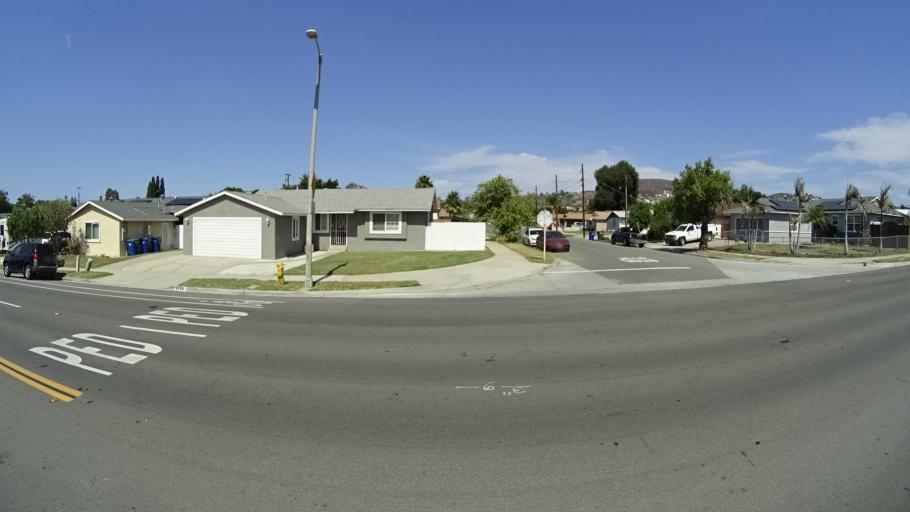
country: US
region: California
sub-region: San Diego County
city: La Presa
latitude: 32.7077
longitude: -117.0045
